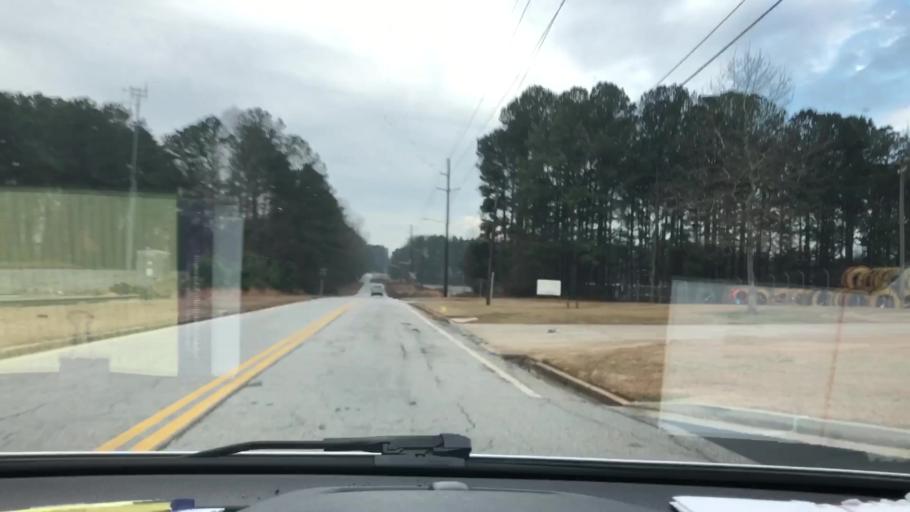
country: US
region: Georgia
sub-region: Gwinnett County
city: Berkeley Lake
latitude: 33.9752
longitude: -84.1685
